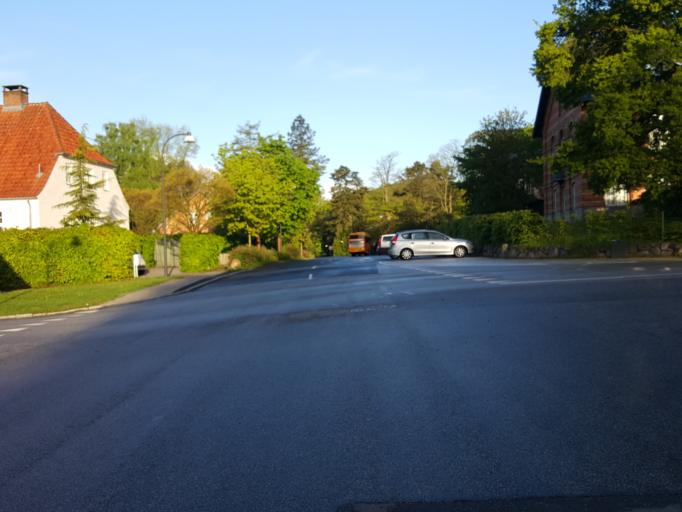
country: DK
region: Capital Region
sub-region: Rudersdal Kommune
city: Holte
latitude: 55.8465
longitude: 12.4633
